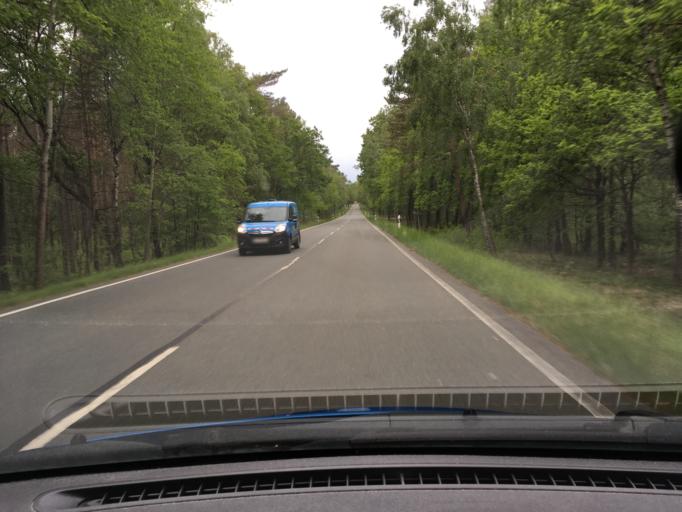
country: DE
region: Lower Saxony
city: Bispingen
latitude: 53.0924
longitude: 10.0382
